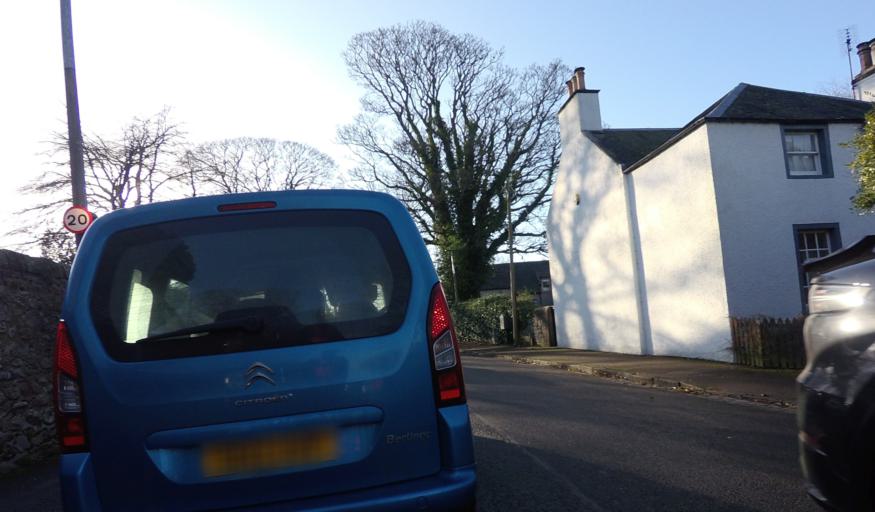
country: GB
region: Scotland
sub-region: Fife
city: Aberdour
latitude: 55.9776
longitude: -3.3005
